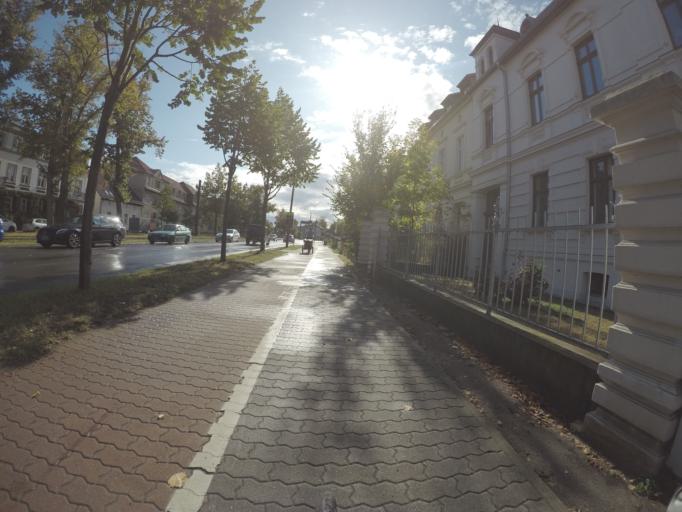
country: DE
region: Brandenburg
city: Strausberg
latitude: 52.5726
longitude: 13.8771
